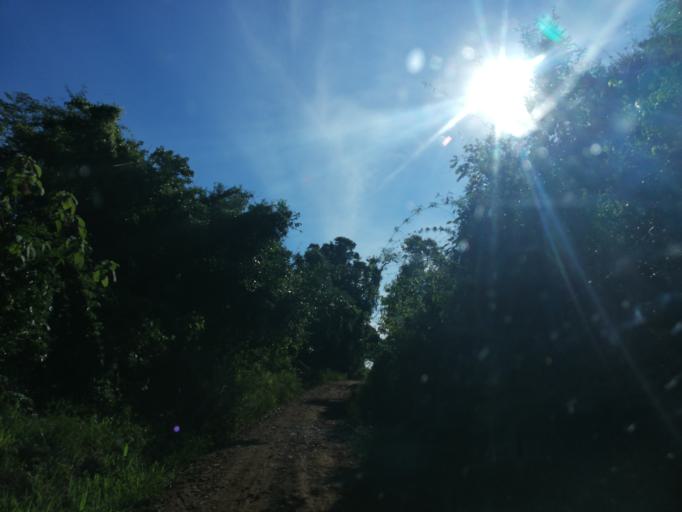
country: AR
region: Misiones
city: Dos de Mayo
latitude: -27.0153
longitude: -54.4278
